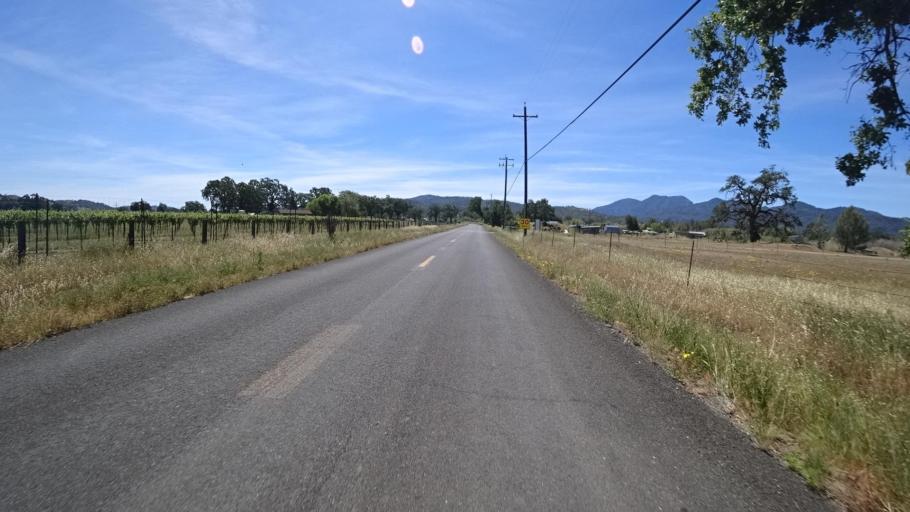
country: US
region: California
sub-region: Lake County
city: Middletown
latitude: 38.7637
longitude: -122.6183
